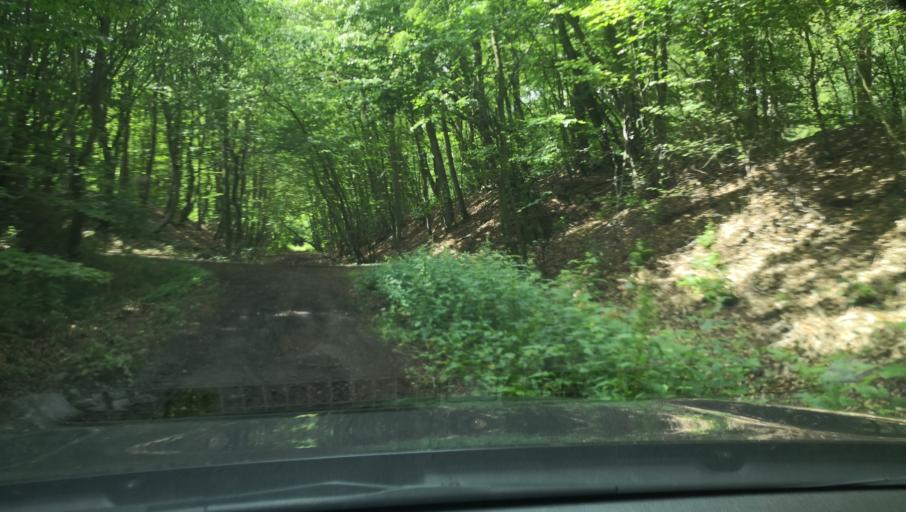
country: SE
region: Skane
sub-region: Tomelilla Kommun
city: Tomelilla
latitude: 55.6108
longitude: 14.1002
